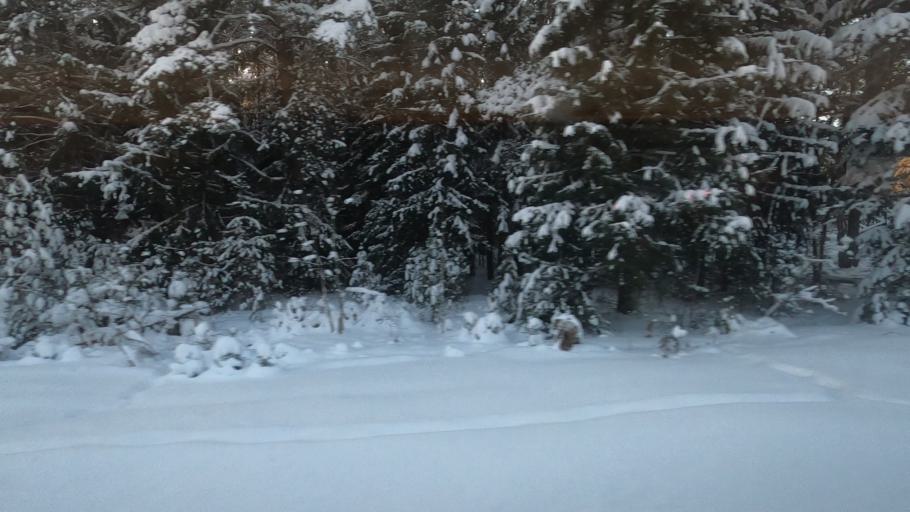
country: RU
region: Moskovskaya
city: Novo-Nikol'skoye
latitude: 56.5535
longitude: 37.5646
